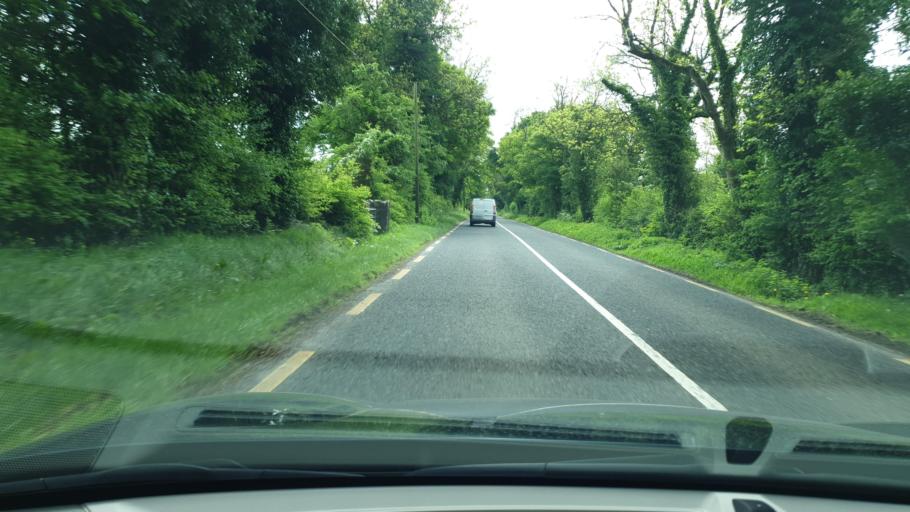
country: IE
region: Ulster
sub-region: An Cabhan
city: Kingscourt
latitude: 53.8427
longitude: -6.7720
